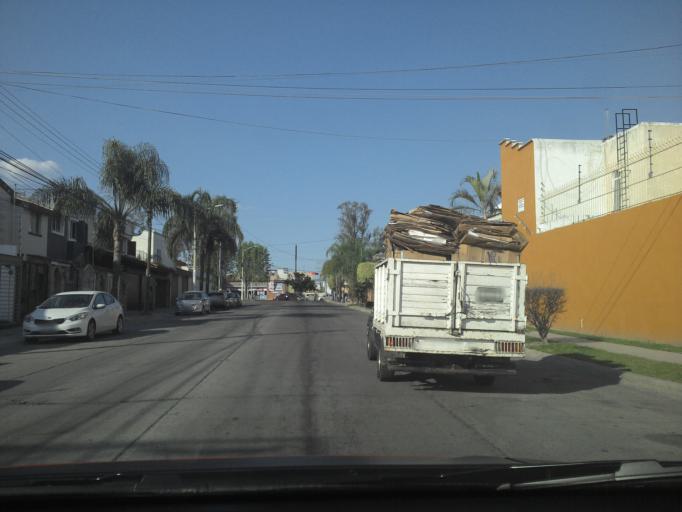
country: MX
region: Jalisco
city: Guadalajara
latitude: 20.6578
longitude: -103.4426
